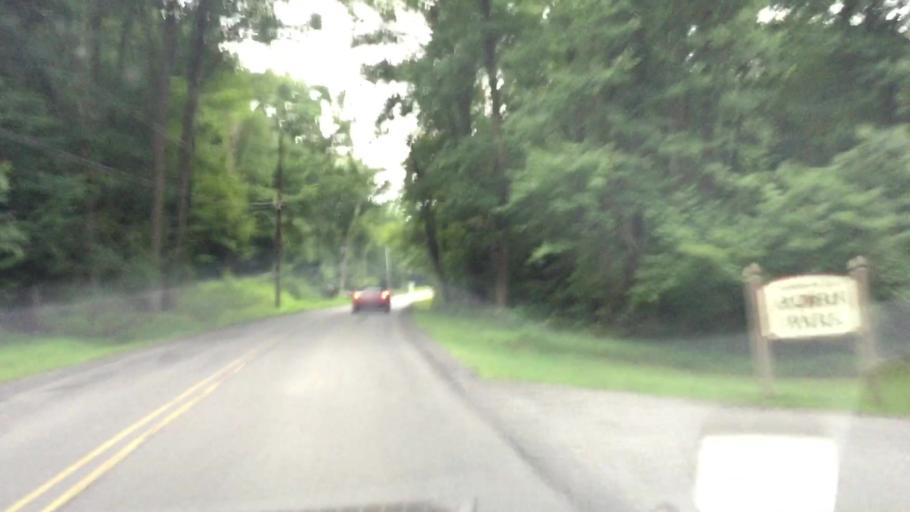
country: US
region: Pennsylvania
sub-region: Allegheny County
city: Franklin Park
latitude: 40.5842
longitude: -80.1174
